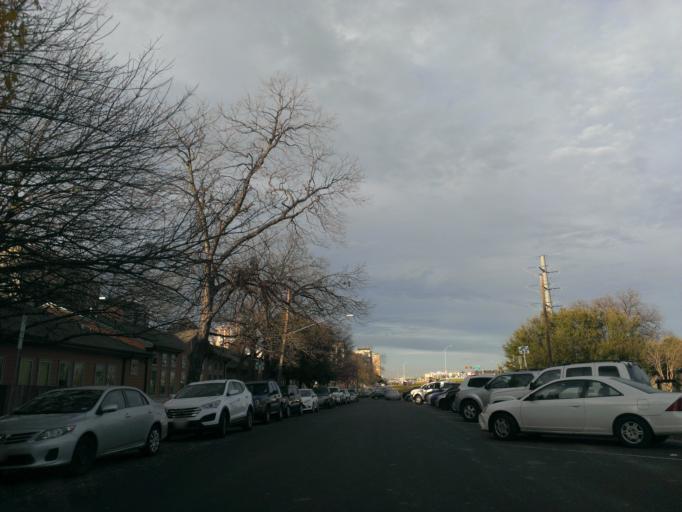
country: US
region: Texas
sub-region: Travis County
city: Austin
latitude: 30.2564
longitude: -97.7386
